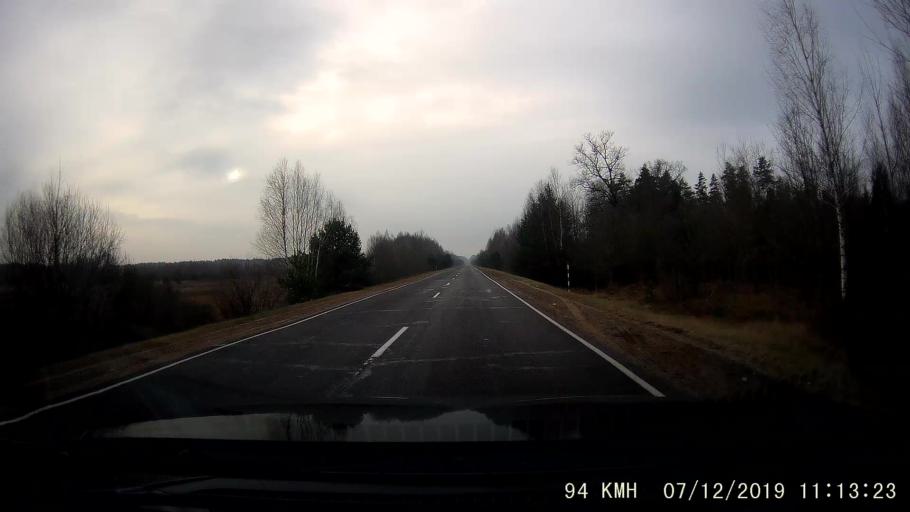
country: BY
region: Grodnenskaya
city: Iwye
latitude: 53.8752
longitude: 25.7398
